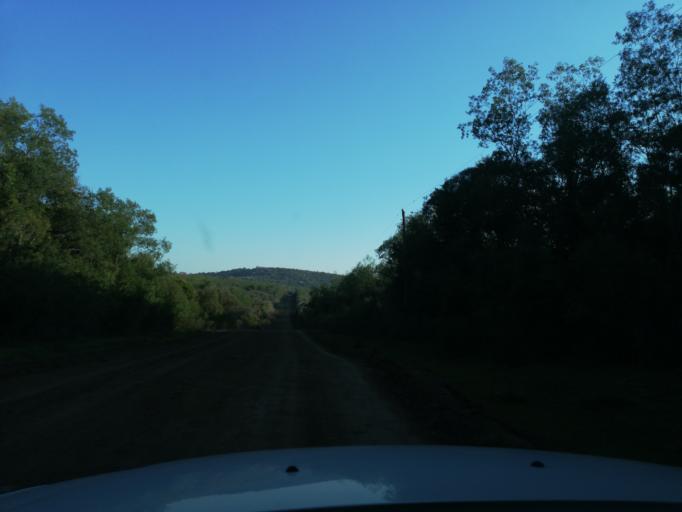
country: AR
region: Misiones
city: Cerro Cora
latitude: -27.5976
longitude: -55.6971
